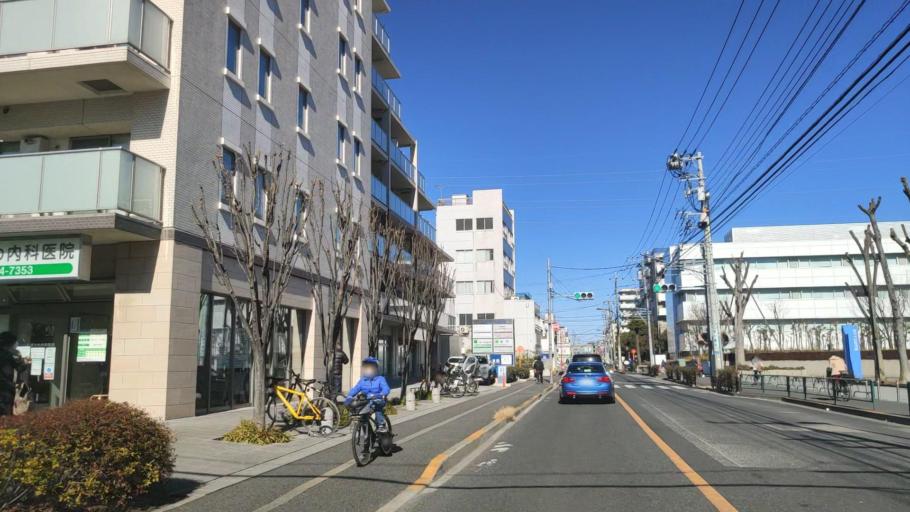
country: JP
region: Tokyo
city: Mitaka-shi
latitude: 35.6876
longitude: 139.5688
